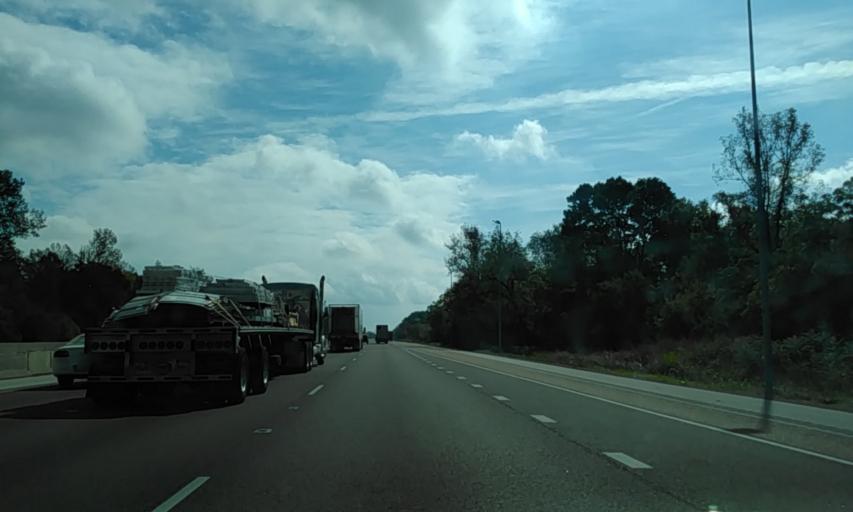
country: US
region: Illinois
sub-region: Saint Clair County
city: Caseyville
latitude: 38.6072
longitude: -90.0303
